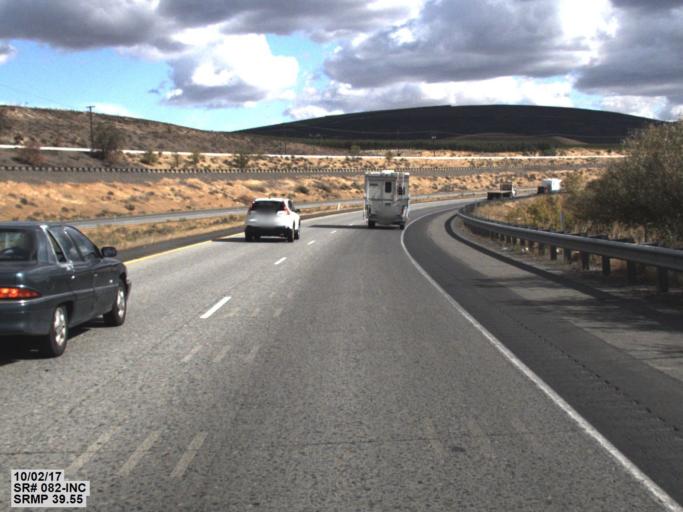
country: US
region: Washington
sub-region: Yakima County
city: Union Gap
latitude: 46.5200
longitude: -120.4620
